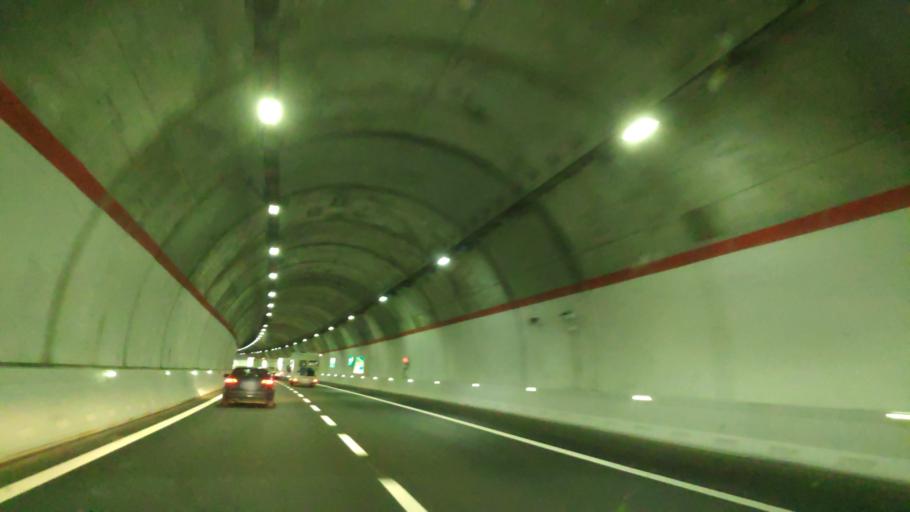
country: IT
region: Campania
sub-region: Provincia di Salerno
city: Casalbuono
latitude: 40.2241
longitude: 15.6719
